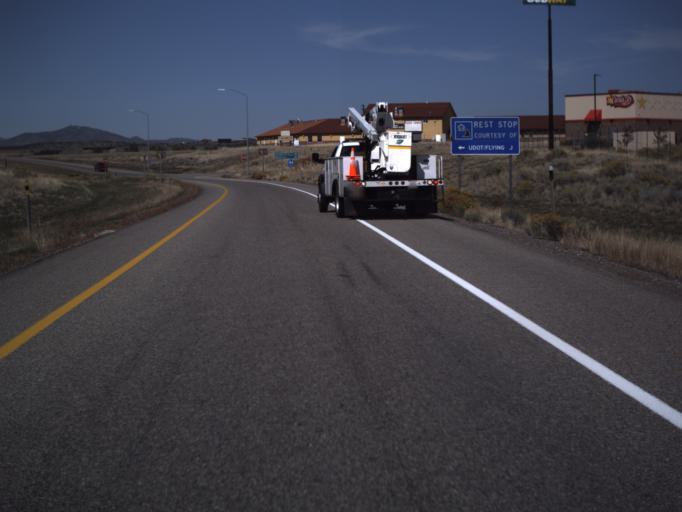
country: US
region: Utah
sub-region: Beaver County
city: Beaver
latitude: 38.2916
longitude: -112.6501
